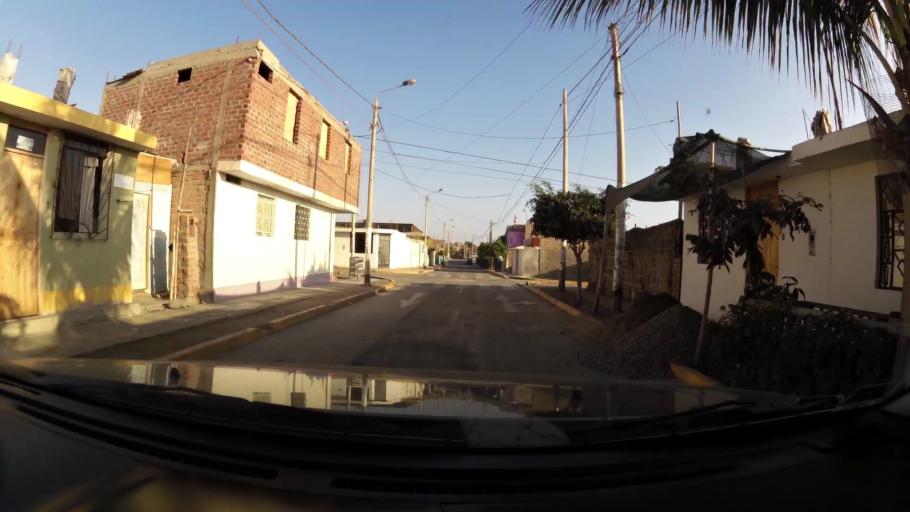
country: PE
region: Ica
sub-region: Provincia de Pisco
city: Villa Tupac Amaru
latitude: -13.7069
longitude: -76.1495
